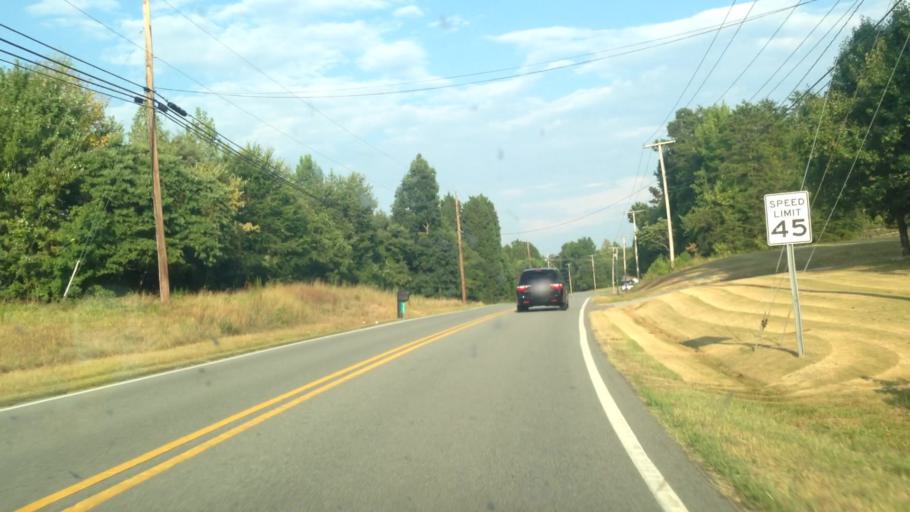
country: US
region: North Carolina
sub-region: Guilford County
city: High Point
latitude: 35.9406
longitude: -80.0634
